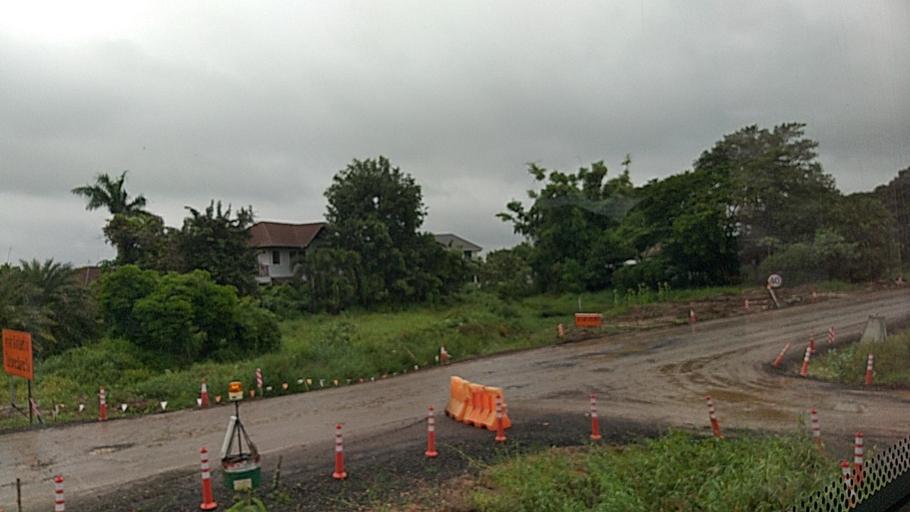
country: TH
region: Nakhon Ratchasima
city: Nakhon Ratchasima
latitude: 14.9904
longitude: 102.0610
